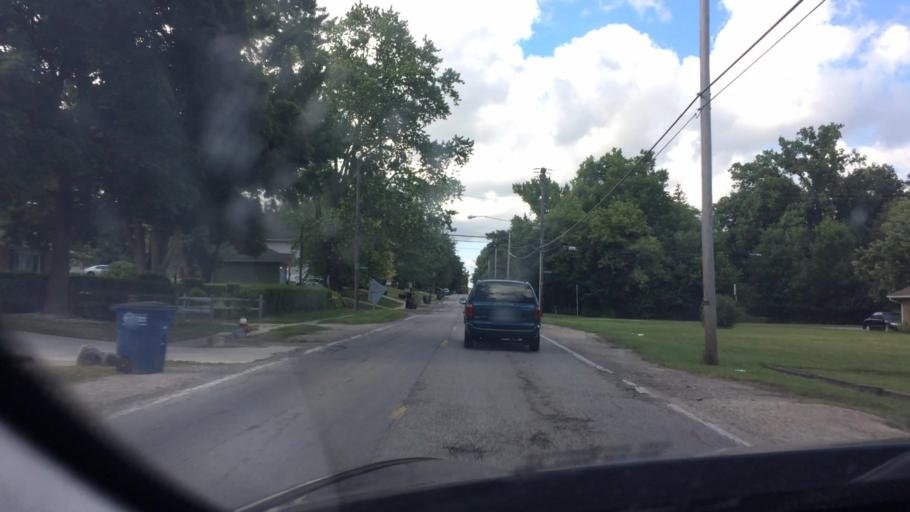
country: US
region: Ohio
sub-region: Lucas County
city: Ottawa Hills
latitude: 41.6496
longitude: -83.6407
